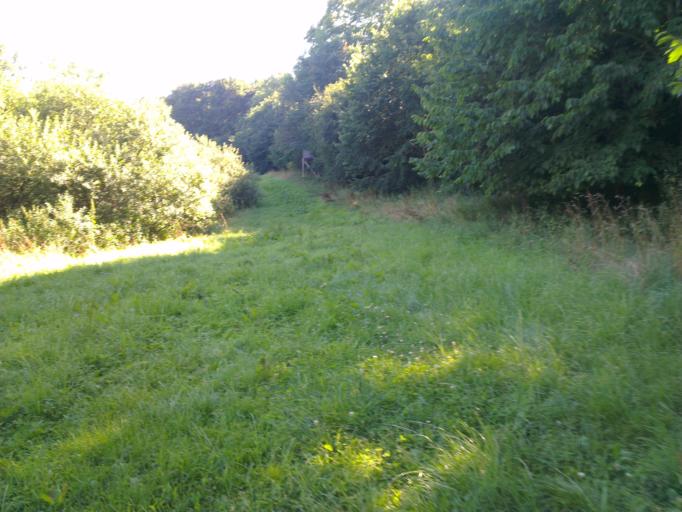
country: DK
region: Capital Region
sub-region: Frederikssund Kommune
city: Skibby
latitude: 55.7713
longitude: 12.0283
